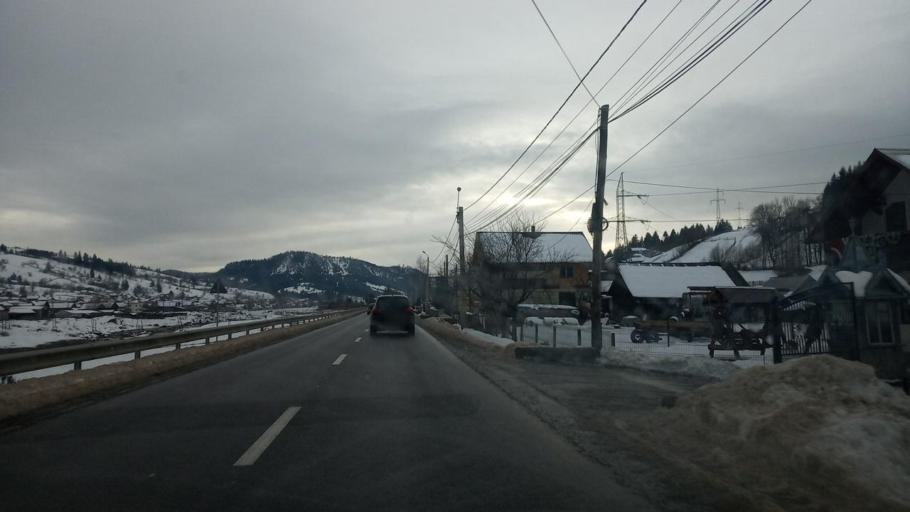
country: RO
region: Suceava
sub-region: Comuna Frasin
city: Frasin
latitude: 47.5102
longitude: 25.7984
